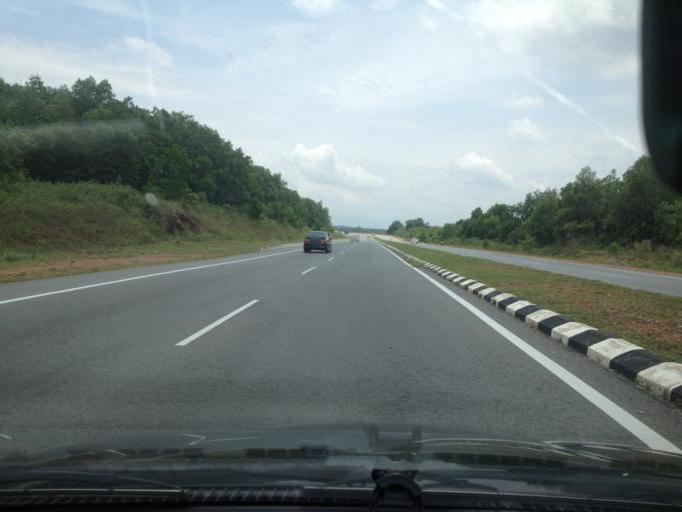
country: MY
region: Kedah
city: Sungai Petani
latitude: 5.6143
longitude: 100.5608
